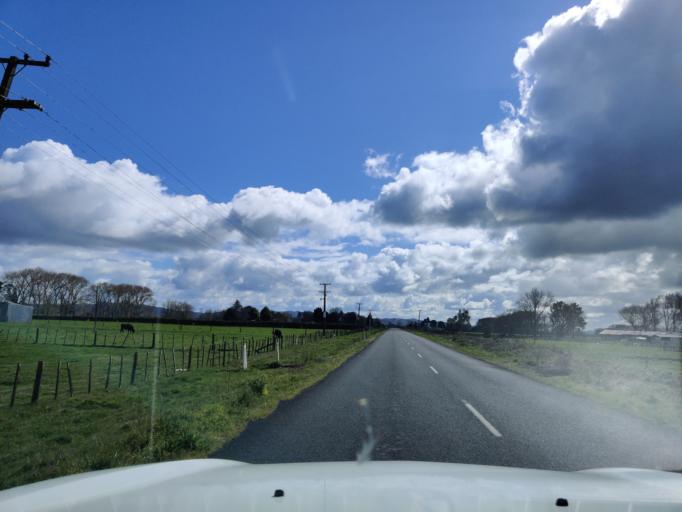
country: NZ
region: Waikato
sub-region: Waikato District
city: Ngaruawahia
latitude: -37.5977
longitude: 175.2973
